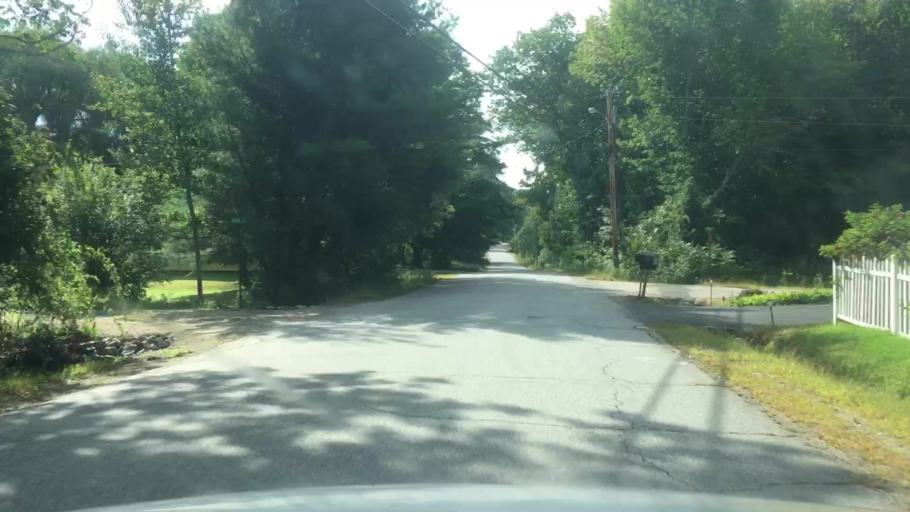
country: US
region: Maine
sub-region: Kennebec County
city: Gardiner
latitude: 44.1760
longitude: -69.8220
